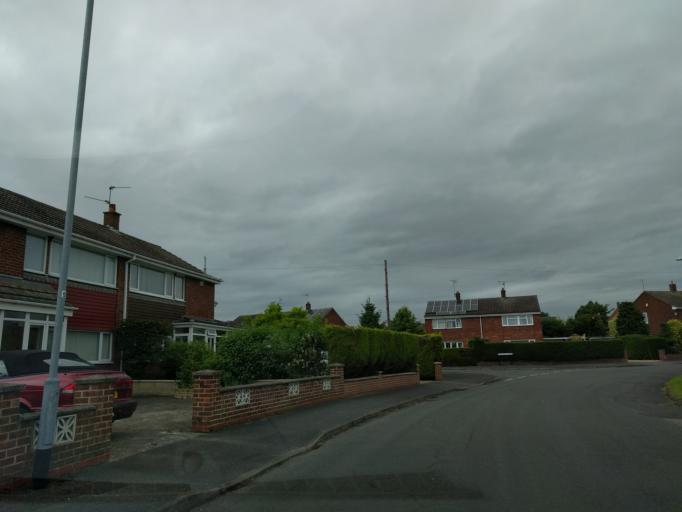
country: GB
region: England
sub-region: Nottinghamshire
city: Newark on Trent
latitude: 53.0518
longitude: -0.7863
